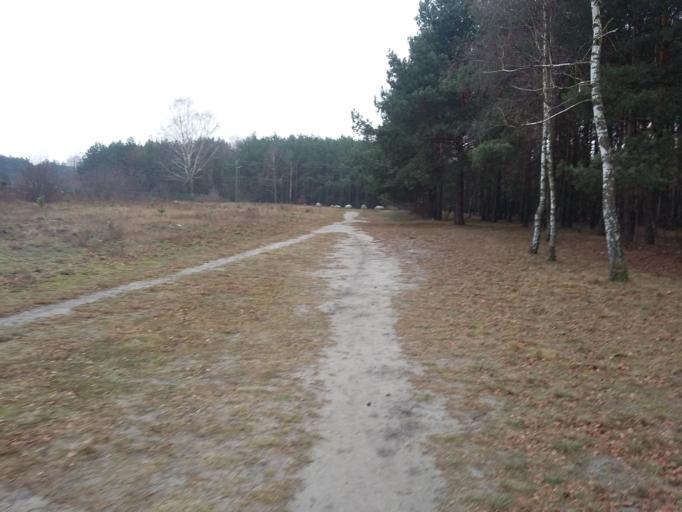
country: PL
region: Lodz Voivodeship
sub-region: Powiat pabianicki
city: Ksawerow
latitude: 51.7283
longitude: 19.3829
